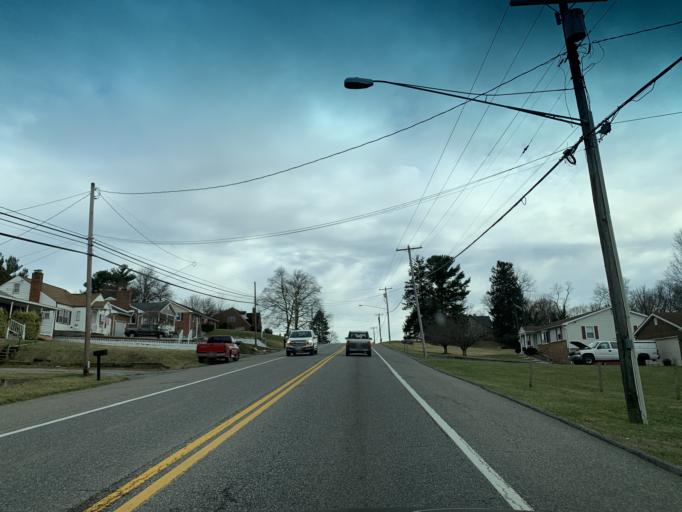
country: US
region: Maryland
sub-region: Washington County
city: Boonsboro
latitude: 39.5171
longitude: -77.6584
